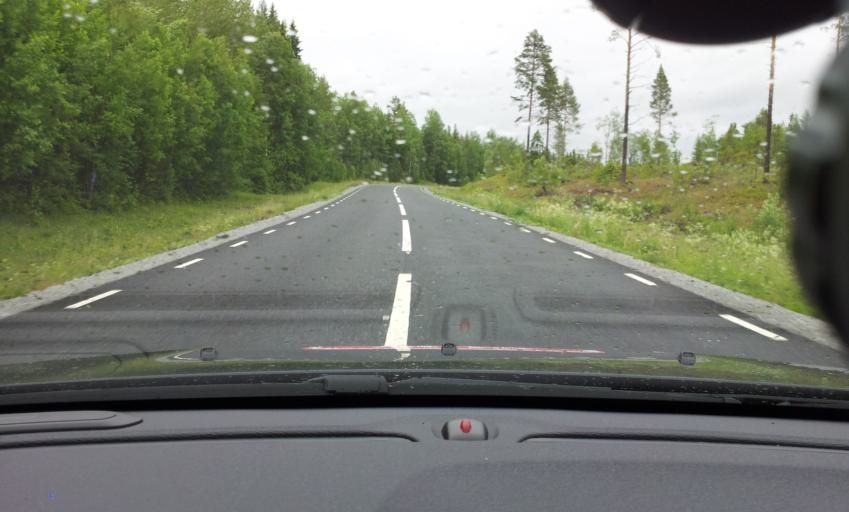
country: SE
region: Jaemtland
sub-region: OEstersunds Kommun
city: Lit
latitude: 63.7359
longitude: 14.8826
